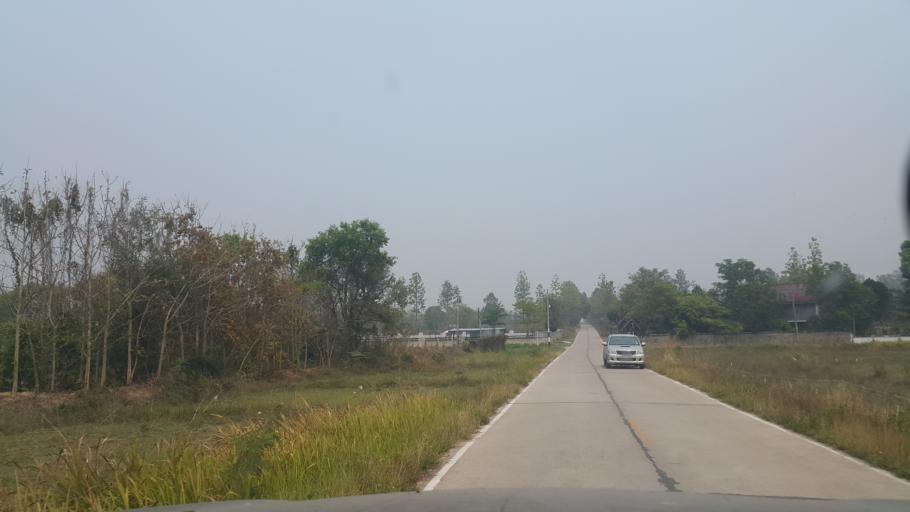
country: TH
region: Lampang
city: Hang Chat
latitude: 18.2757
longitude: 99.2622
